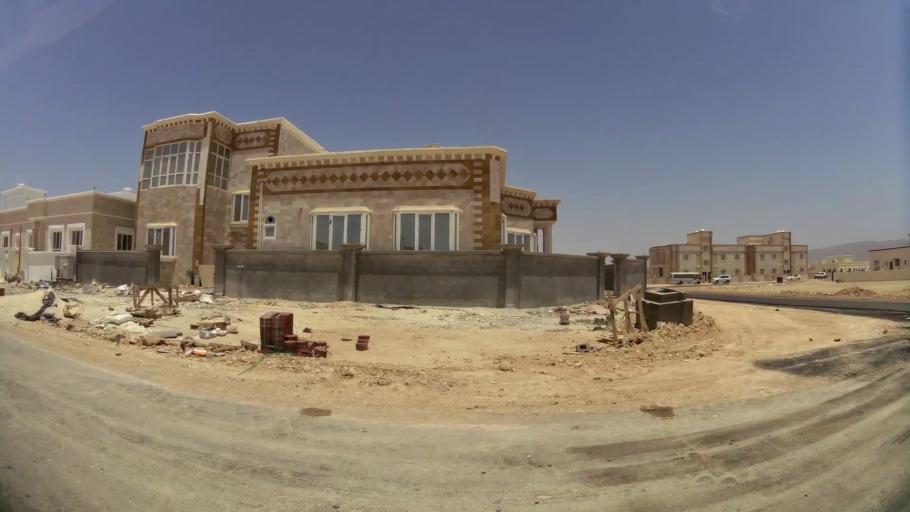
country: OM
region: Zufar
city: Salalah
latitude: 17.0988
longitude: 54.1678
